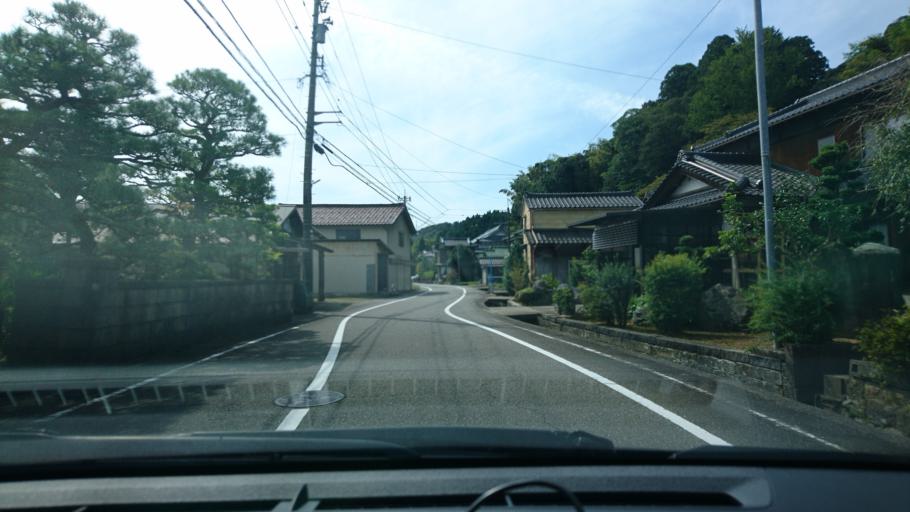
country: JP
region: Fukui
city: Maruoka
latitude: 36.2876
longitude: 136.2948
